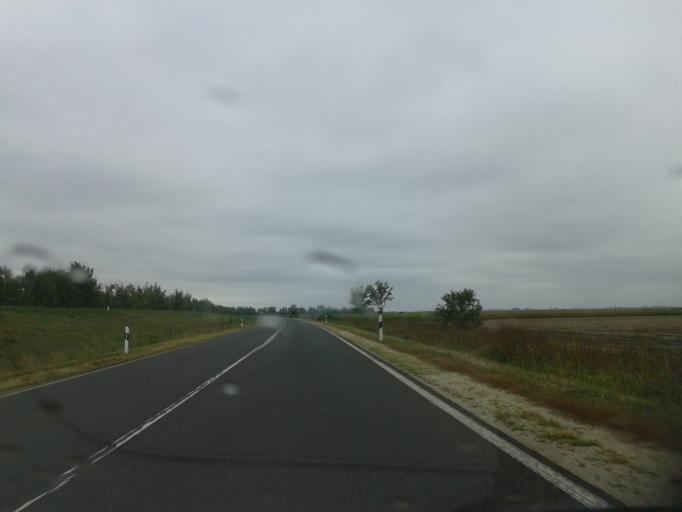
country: HU
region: Tolna
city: Bolcske
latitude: 46.7443
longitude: 19.0108
